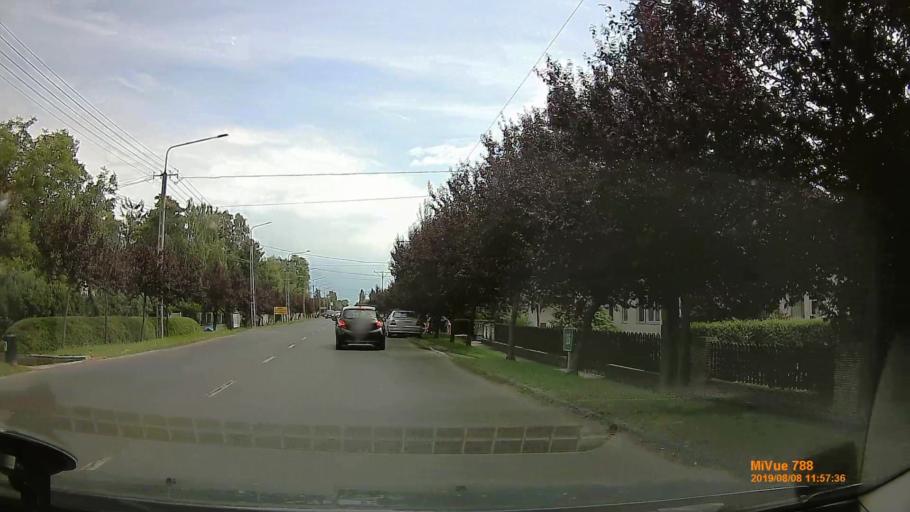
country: HU
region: Somogy
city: Balatonlelle
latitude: 46.7884
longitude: 17.7015
